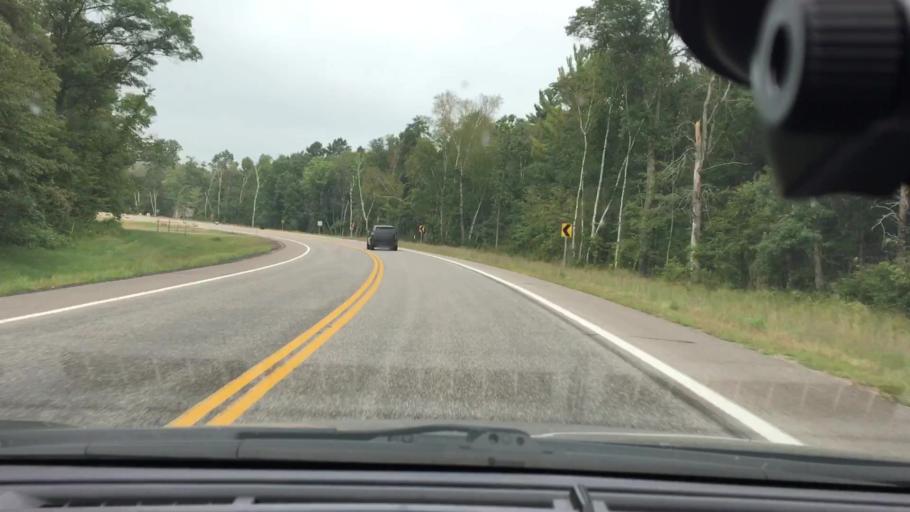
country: US
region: Minnesota
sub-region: Crow Wing County
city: Cross Lake
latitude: 46.6656
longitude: -94.0395
